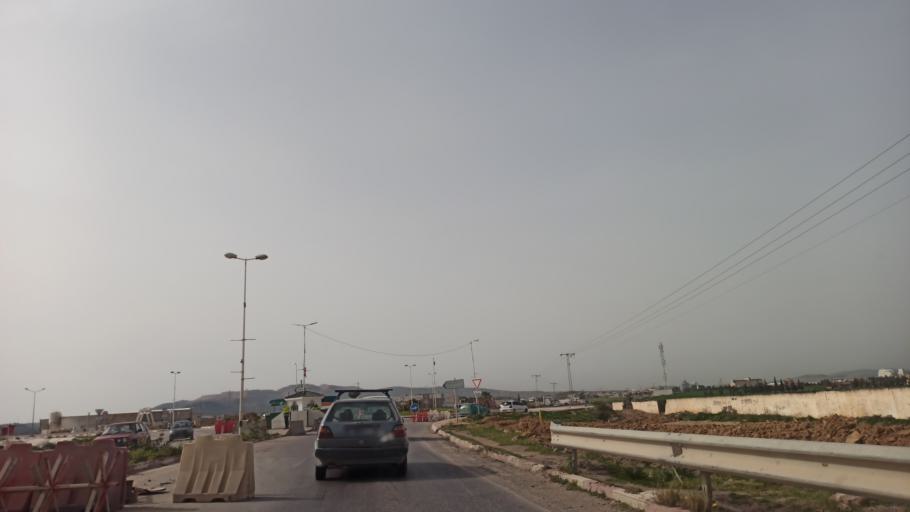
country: TN
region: Tunis
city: La Mohammedia
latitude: 36.5654
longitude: 10.0829
